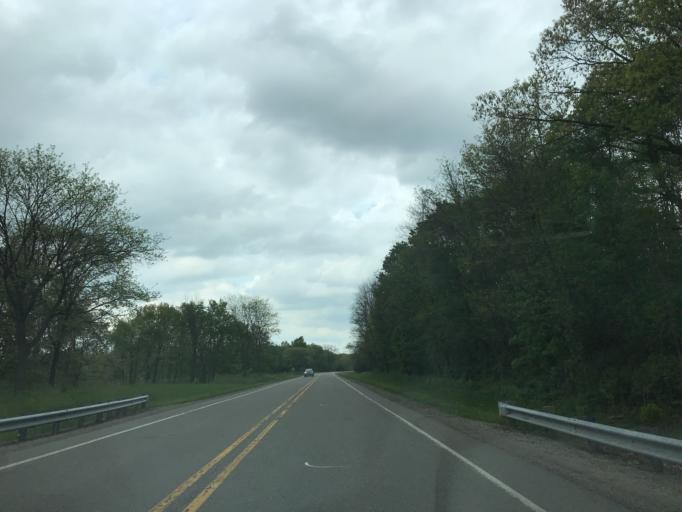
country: US
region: Michigan
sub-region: Oakland County
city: Milford
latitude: 42.5317
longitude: -83.6327
